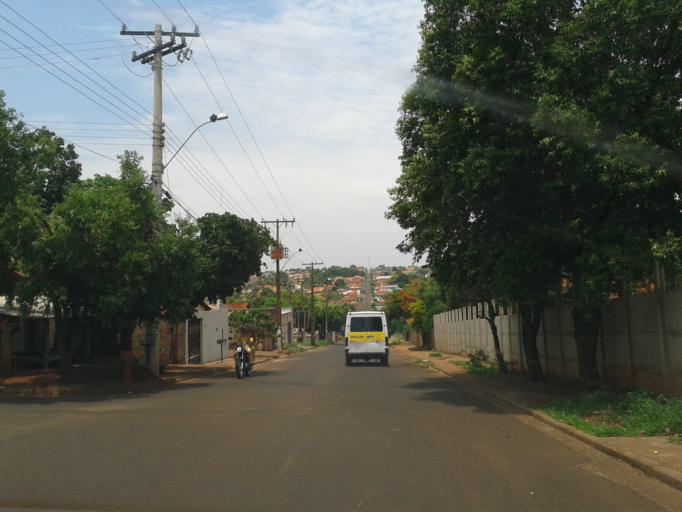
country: BR
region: Minas Gerais
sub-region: Ituiutaba
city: Ituiutaba
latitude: -18.9909
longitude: -49.4379
